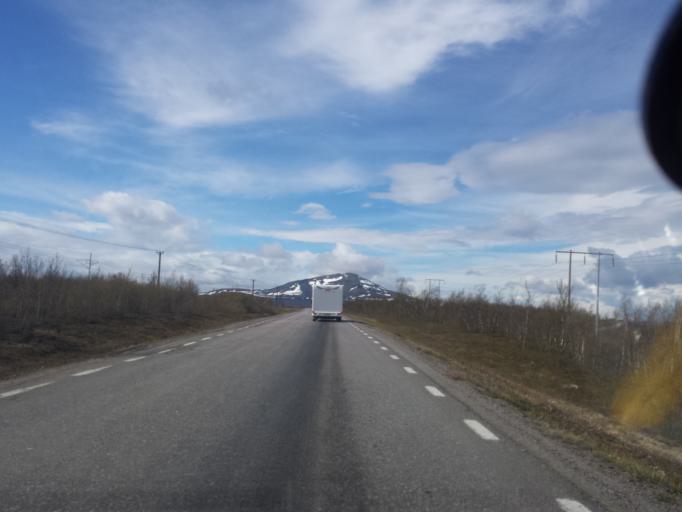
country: SE
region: Norrbotten
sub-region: Kiruna Kommun
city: Kiruna
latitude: 68.1141
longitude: 19.8310
